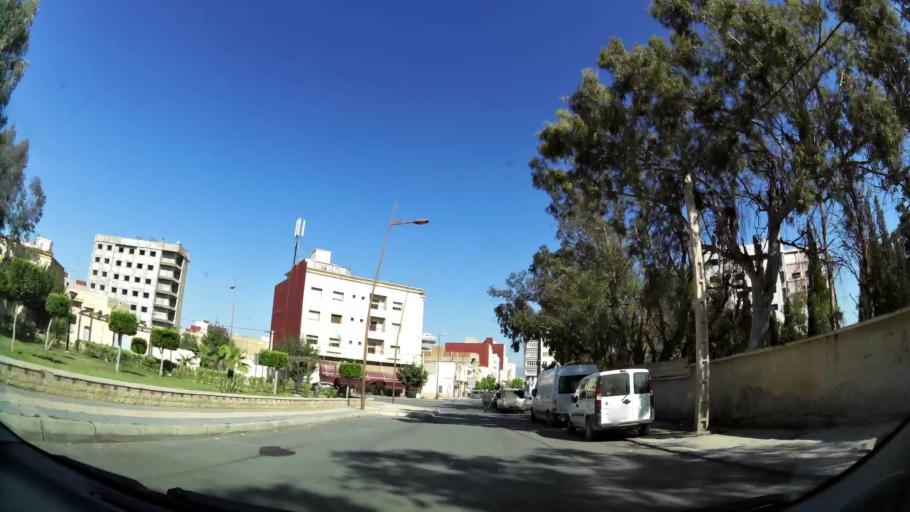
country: MA
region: Oriental
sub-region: Oujda-Angad
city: Oujda
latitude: 34.6860
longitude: -1.9207
